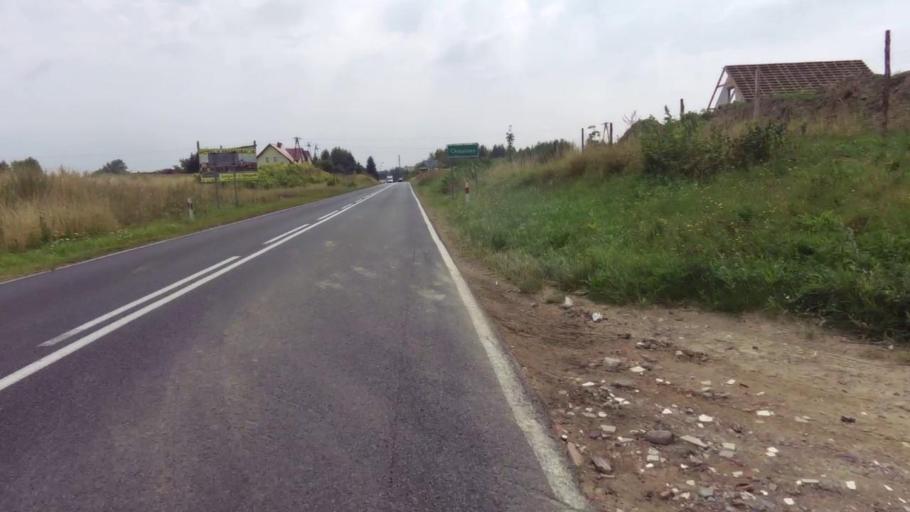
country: PL
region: West Pomeranian Voivodeship
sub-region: Powiat choszczenski
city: Choszczno
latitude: 53.1801
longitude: 15.4057
